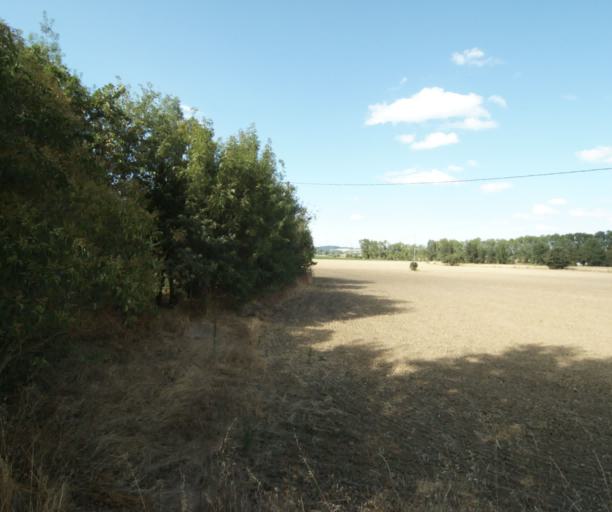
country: FR
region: Midi-Pyrenees
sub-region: Departement de la Haute-Garonne
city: Revel
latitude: 43.5172
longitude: 1.9562
